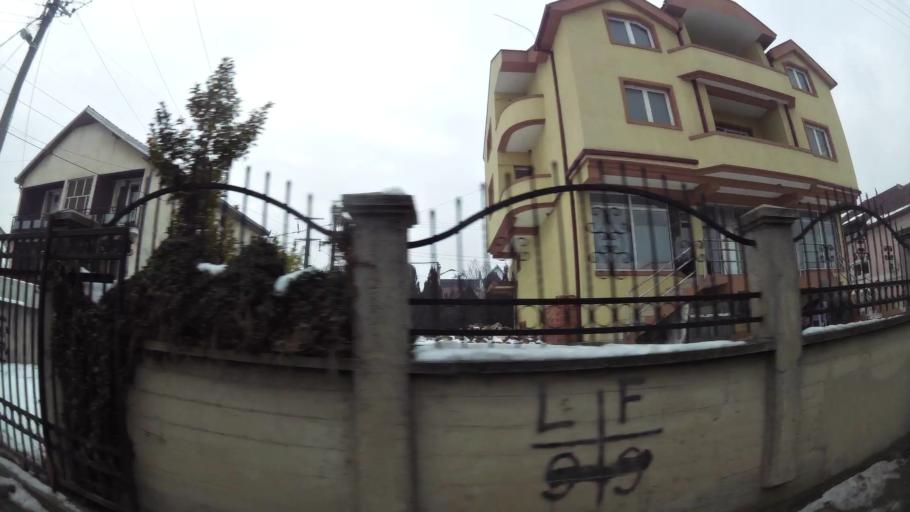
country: MK
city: Kondovo
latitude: 42.0403
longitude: 21.3476
